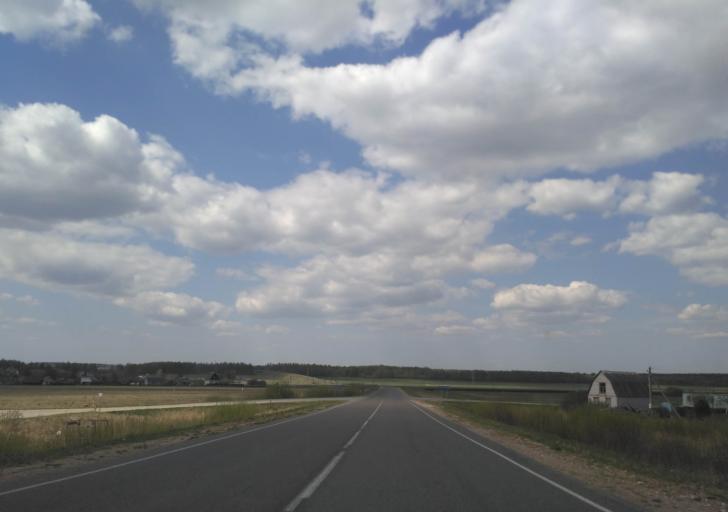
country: BY
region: Minsk
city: Vilyeyka
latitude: 54.5186
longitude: 26.9768
